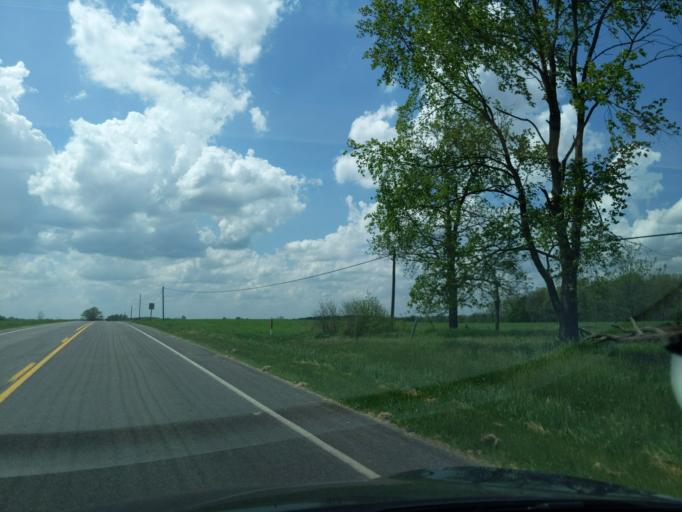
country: US
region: Michigan
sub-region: Ingham County
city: Mason
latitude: 42.5965
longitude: -84.4227
